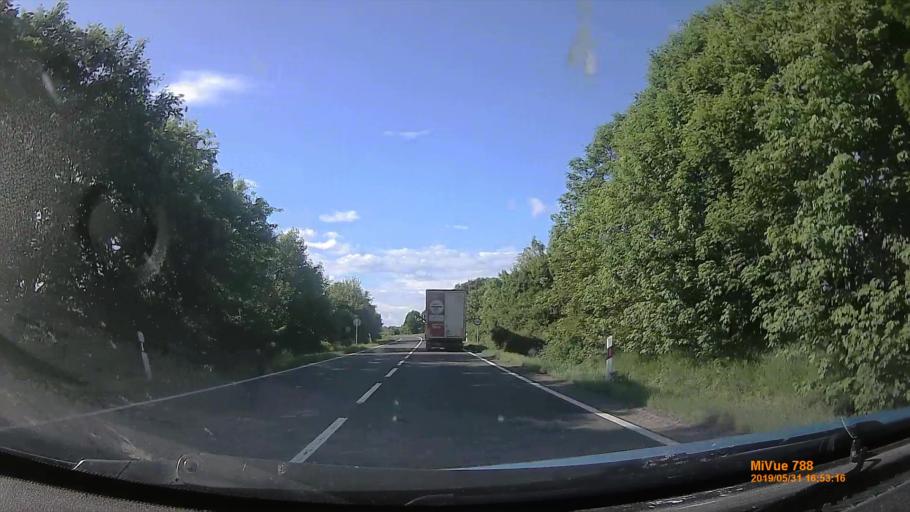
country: HU
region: Nograd
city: Retsag
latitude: 47.9681
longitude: 19.1282
